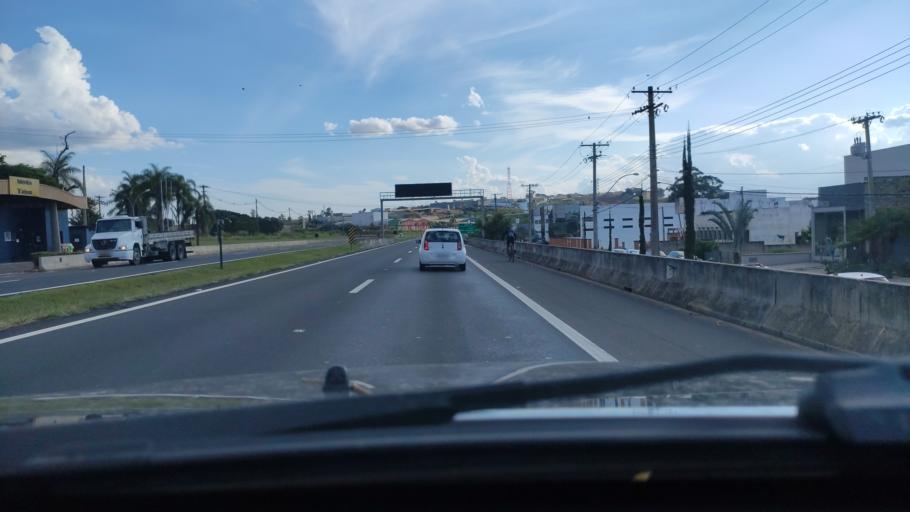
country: BR
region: Sao Paulo
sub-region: Itapira
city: Itapira
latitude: -22.4491
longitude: -46.8370
